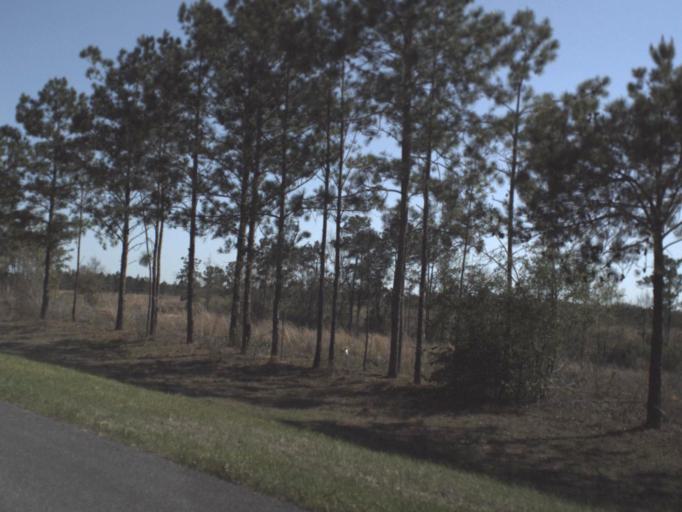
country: US
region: Florida
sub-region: Walton County
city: DeFuniak Springs
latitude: 30.7169
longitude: -86.0191
